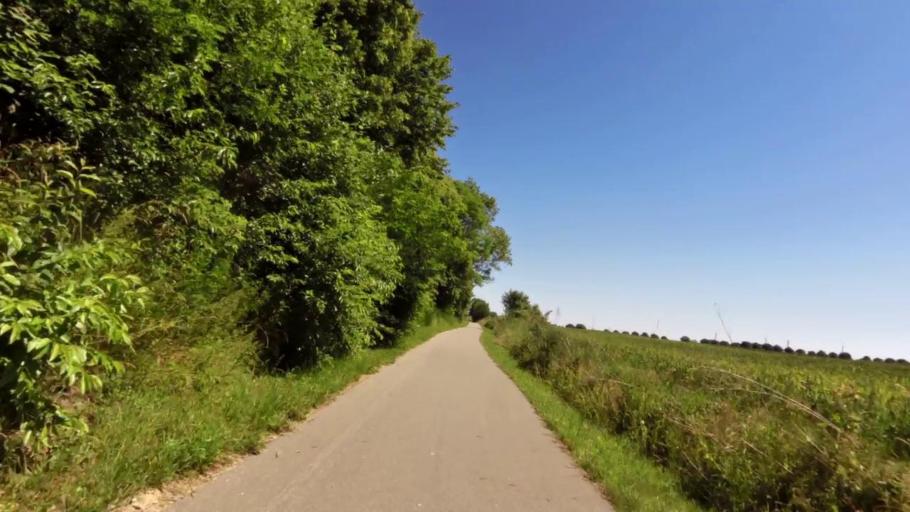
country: PL
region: West Pomeranian Voivodeship
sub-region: Powiat kolobrzeski
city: Goscino
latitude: 54.0403
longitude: 15.6604
